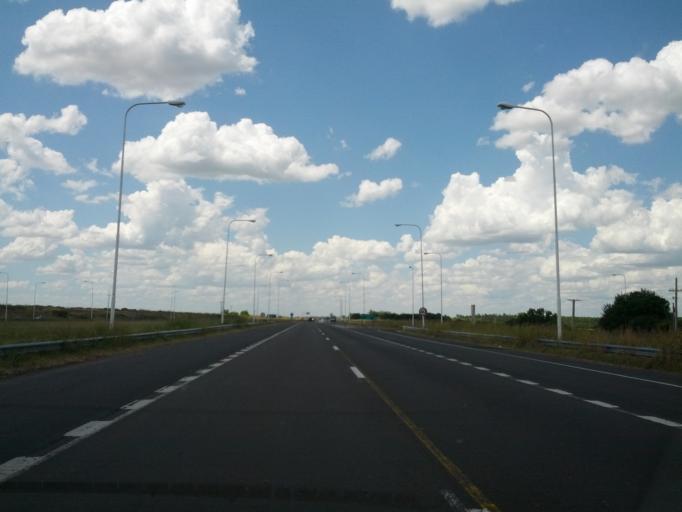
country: AR
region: Entre Rios
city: Concepcion del Uruguay
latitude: -32.5414
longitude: -58.3469
